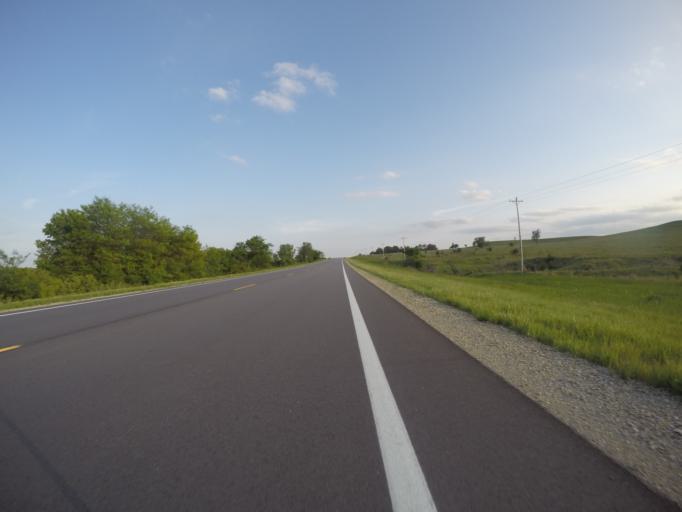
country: US
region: Kansas
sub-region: Pottawatomie County
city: Westmoreland
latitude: 39.4020
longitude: -96.5200
